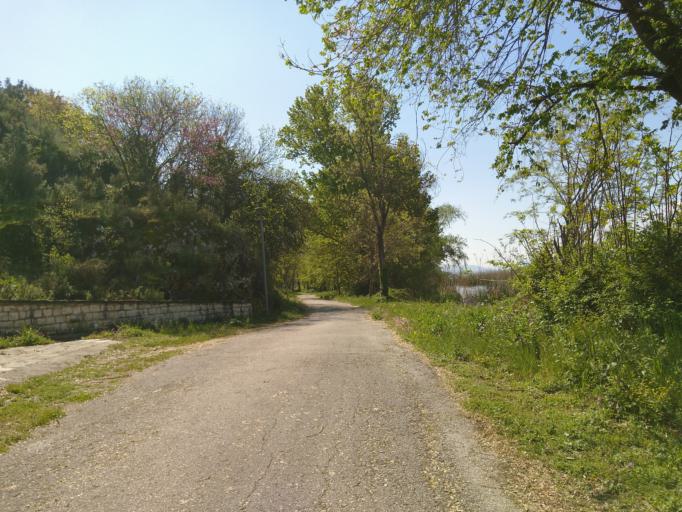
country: GR
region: Epirus
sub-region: Nomos Ioanninon
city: Ioannina
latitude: 39.6784
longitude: 20.8724
